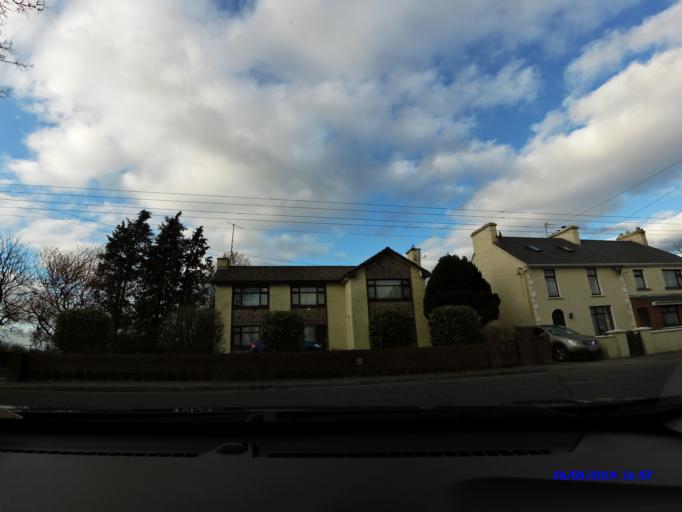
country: IE
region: Connaught
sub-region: Maigh Eo
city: Ballyhaunis
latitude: 53.7647
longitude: -8.7755
